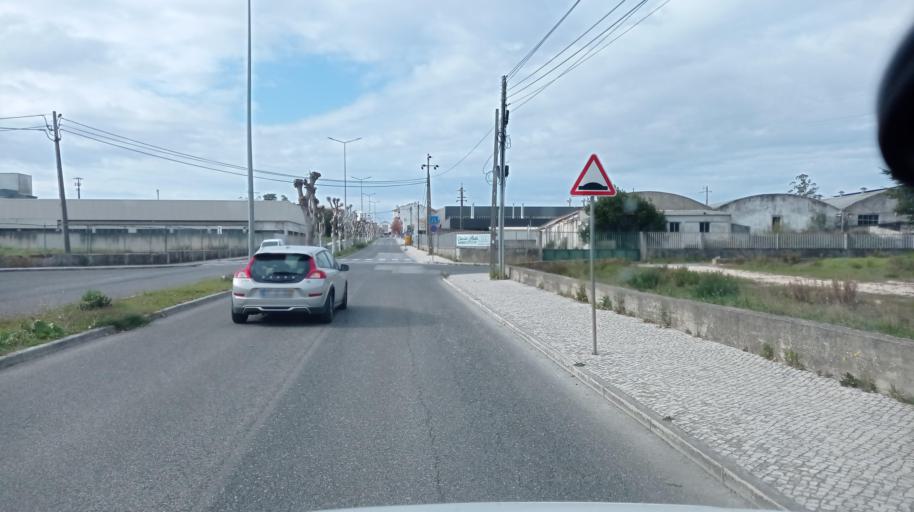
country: PT
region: Leiria
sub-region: Alcobaca
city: Benedita
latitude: 39.4251
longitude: -8.9728
